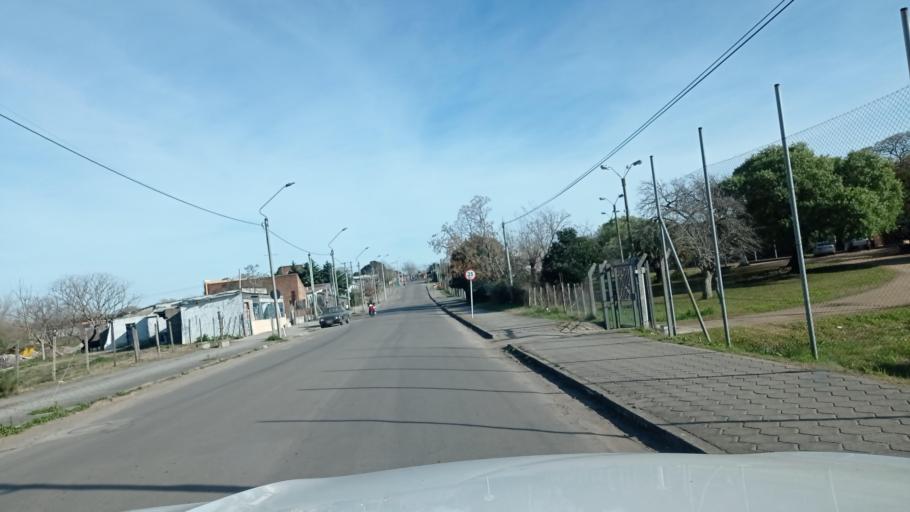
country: UY
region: Florida
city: Florida
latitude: -34.0914
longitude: -56.2246
